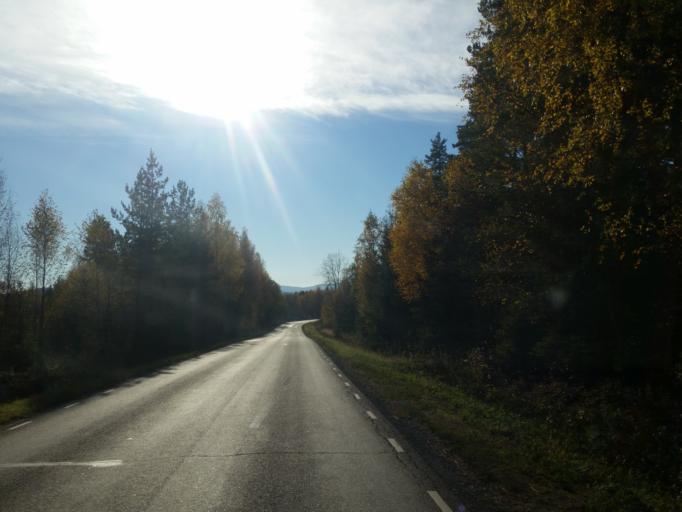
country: SE
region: Dalarna
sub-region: Borlange Kommun
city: Ornas
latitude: 60.5098
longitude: 15.5224
